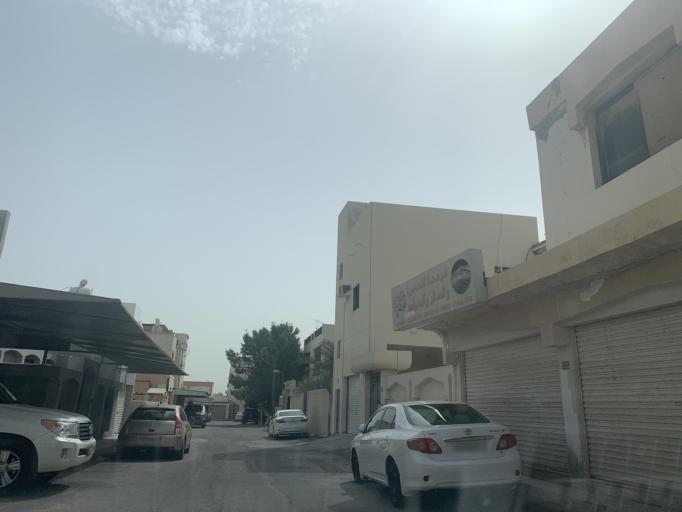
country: BH
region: Northern
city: Ar Rifa'
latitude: 26.1303
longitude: 50.5686
